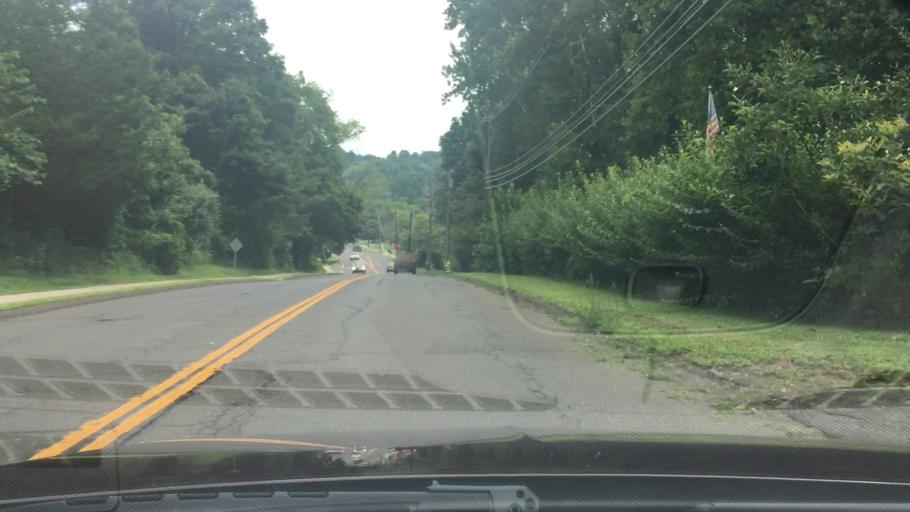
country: US
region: Connecticut
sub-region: Fairfield County
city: Danbury
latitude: 41.4281
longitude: -73.4226
